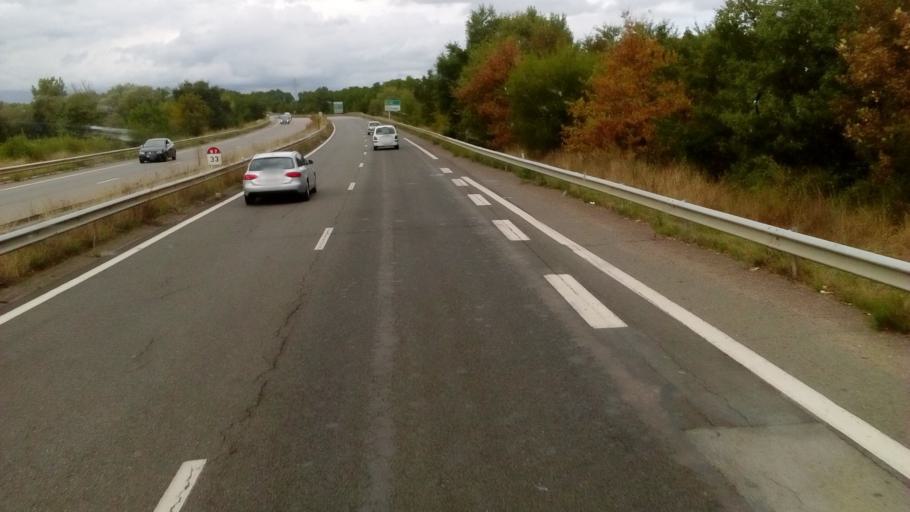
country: FR
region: Rhone-Alpes
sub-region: Departement de la Loire
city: Le Coteau
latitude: 46.0384
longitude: 4.0991
